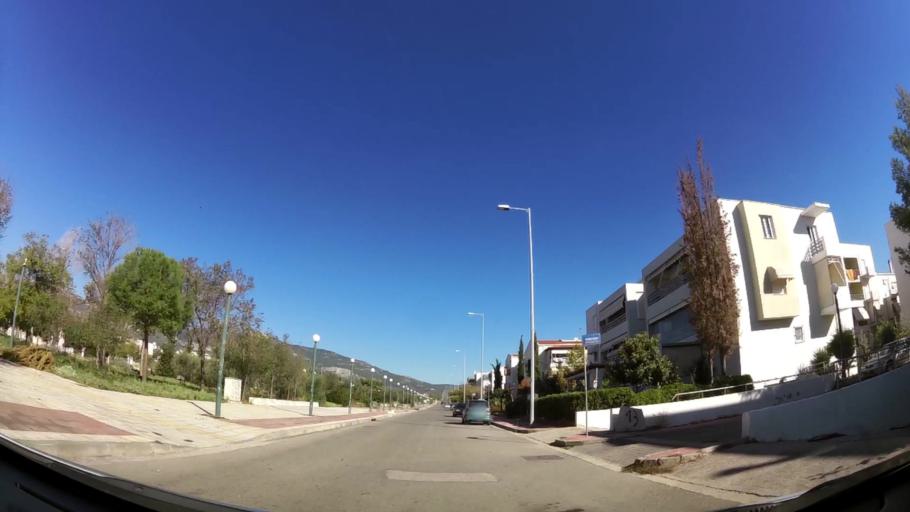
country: GR
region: Attica
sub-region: Nomarchia Anatolikis Attikis
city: Thrakomakedones
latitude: 38.1082
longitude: 23.7690
